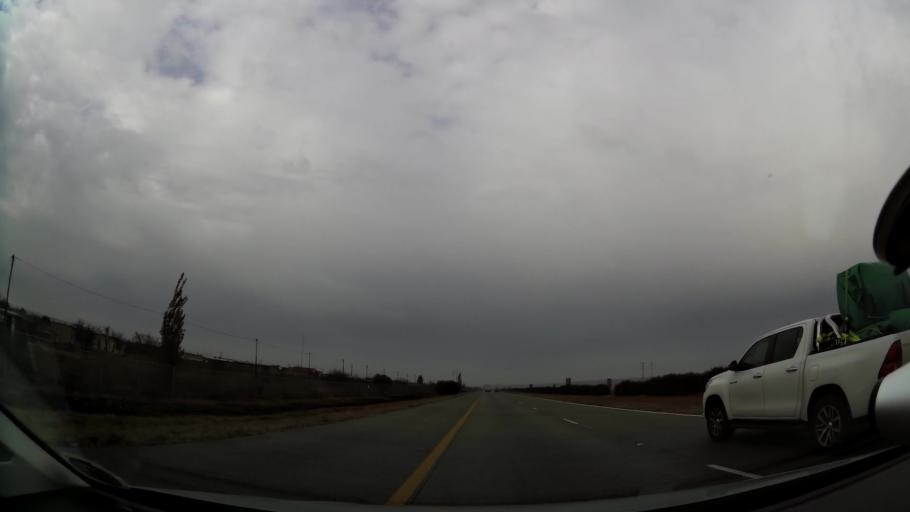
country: ZA
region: Gauteng
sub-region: City of Johannesburg Metropolitan Municipality
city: Orange Farm
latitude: -26.5210
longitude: 27.8104
